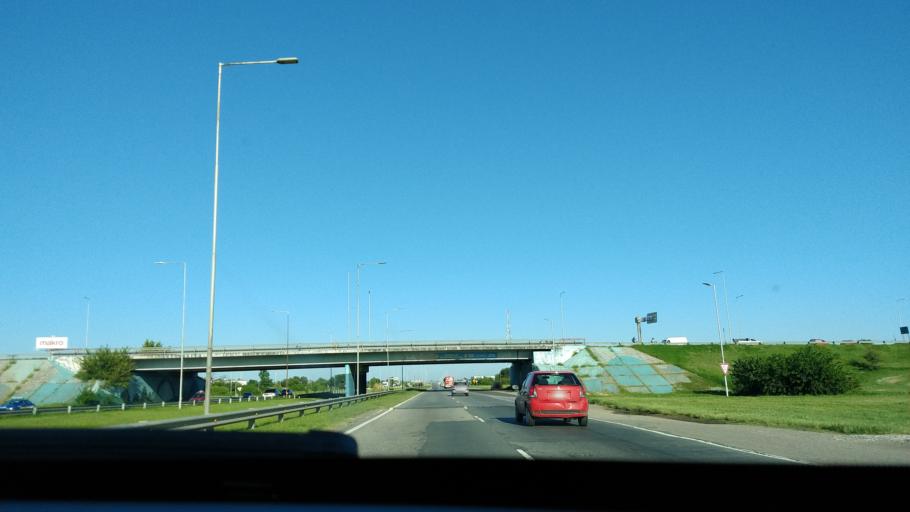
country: AR
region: Cordoba
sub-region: Departamento de Capital
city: Cordoba
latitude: -31.3575
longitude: -64.1774
